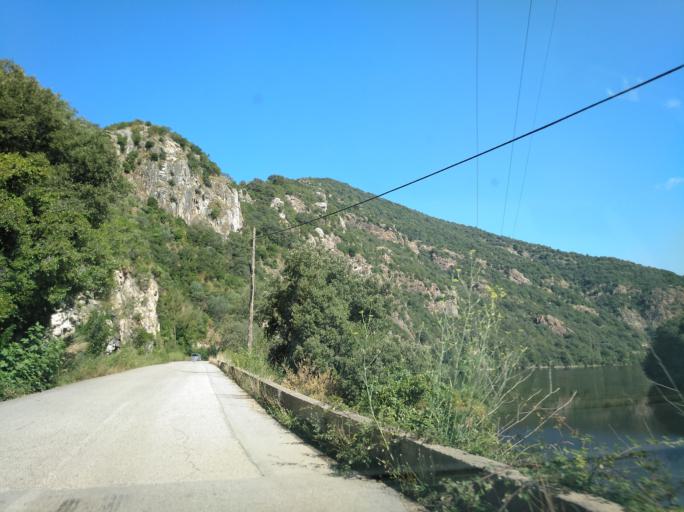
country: ES
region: Catalonia
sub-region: Provincia de Girona
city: la Cellera de Ter
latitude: 41.9782
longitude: 2.5995
